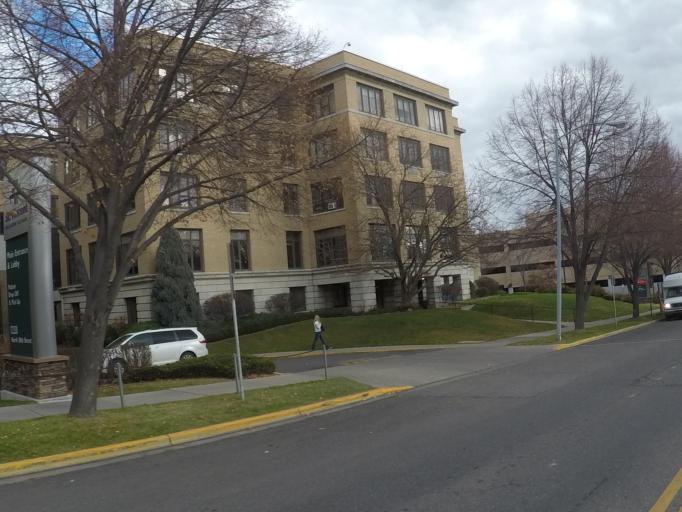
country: US
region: Montana
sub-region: Yellowstone County
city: Billings
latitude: 45.7930
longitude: -108.5201
